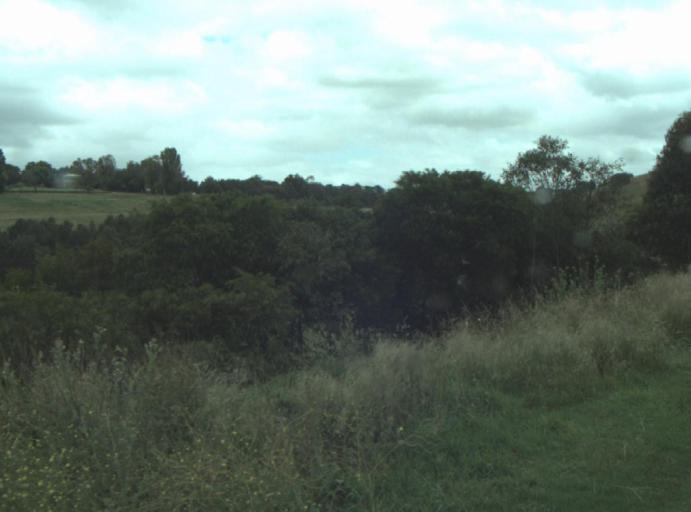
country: AU
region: Victoria
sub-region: Greater Geelong
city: Wandana Heights
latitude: -38.1851
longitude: 144.3012
